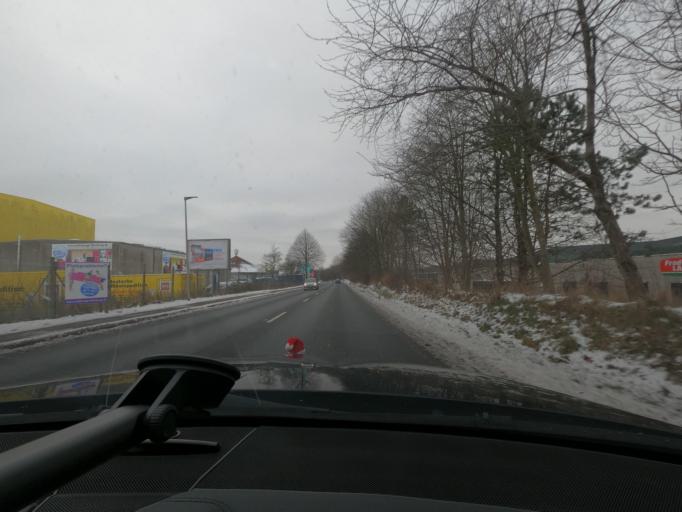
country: DE
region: Schleswig-Holstein
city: Jarplund-Weding
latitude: 54.7622
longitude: 9.4129
